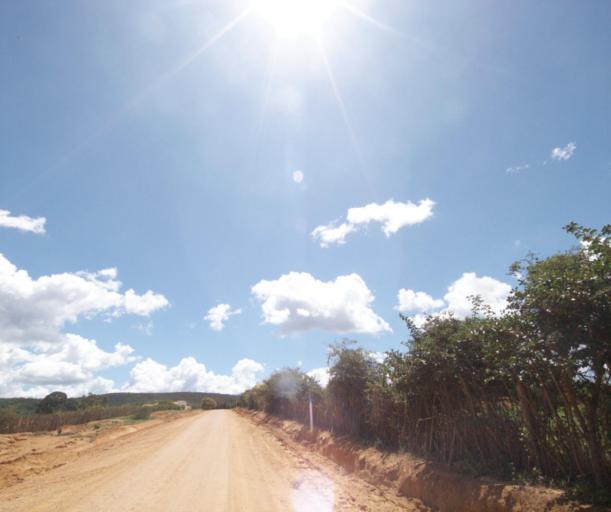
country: BR
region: Bahia
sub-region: Pocoes
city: Pocoes
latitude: -14.3028
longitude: -40.6622
